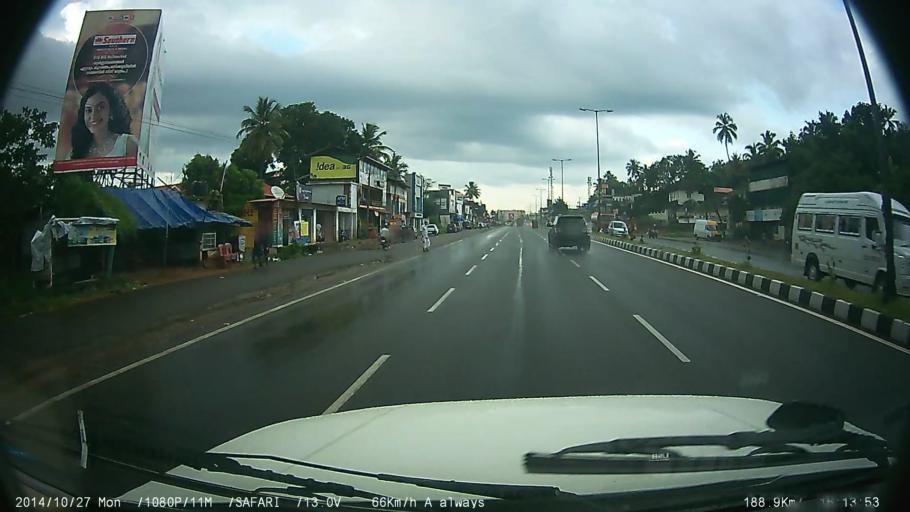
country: IN
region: Kerala
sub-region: Thrissur District
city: Irinjalakuda
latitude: 10.4187
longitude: 76.2702
